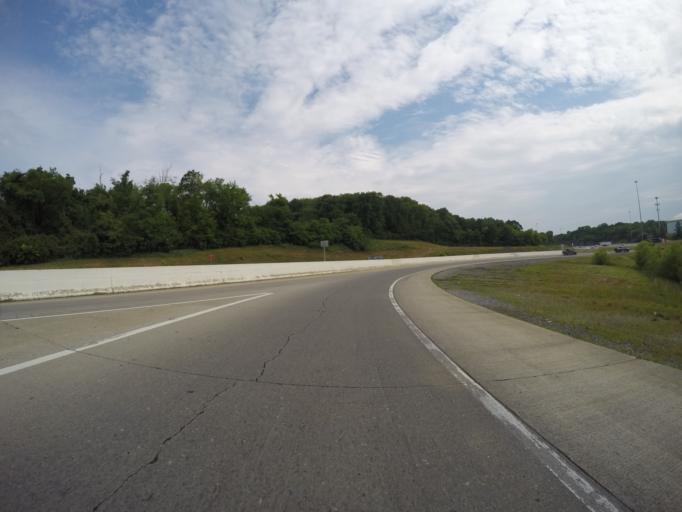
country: US
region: Tennessee
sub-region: Davidson County
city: Goodlettsville
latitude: 36.2658
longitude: -86.7393
